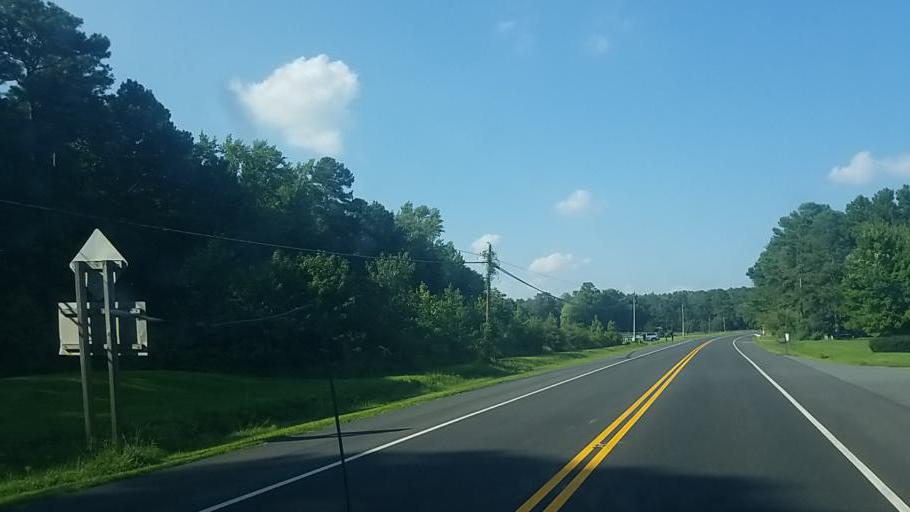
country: US
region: Maryland
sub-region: Worcester County
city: Berlin
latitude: 38.3670
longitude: -75.2004
